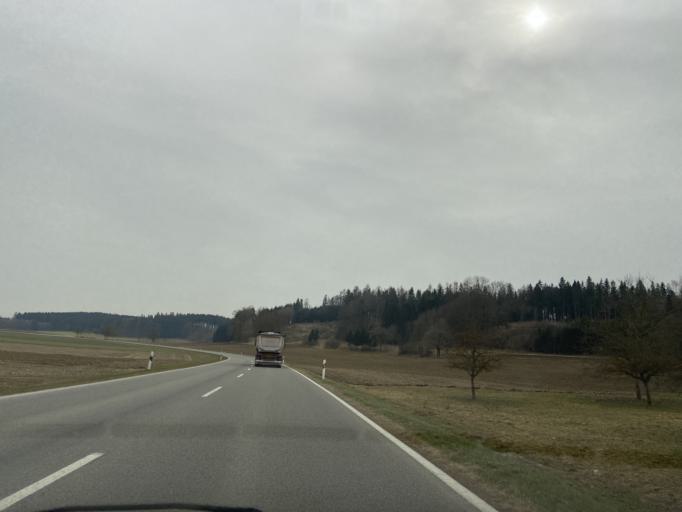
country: DE
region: Baden-Wuerttemberg
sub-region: Tuebingen Region
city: Ostrach
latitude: 47.9705
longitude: 9.3486
